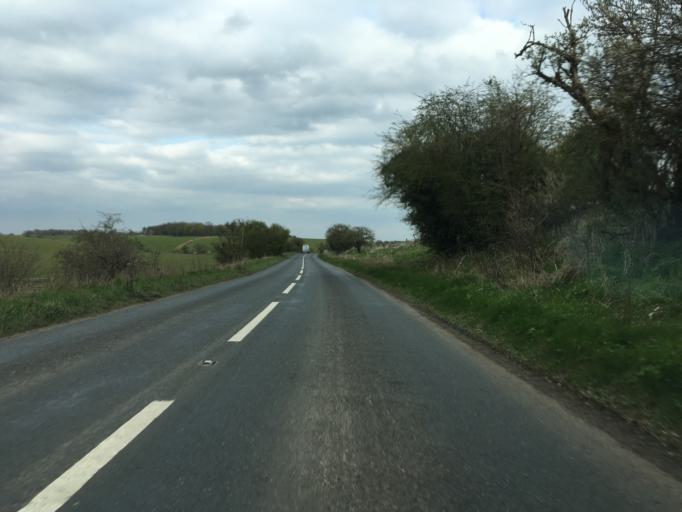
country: GB
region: England
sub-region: Gloucestershire
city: Bourton on the Water
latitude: 51.7886
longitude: -1.7620
